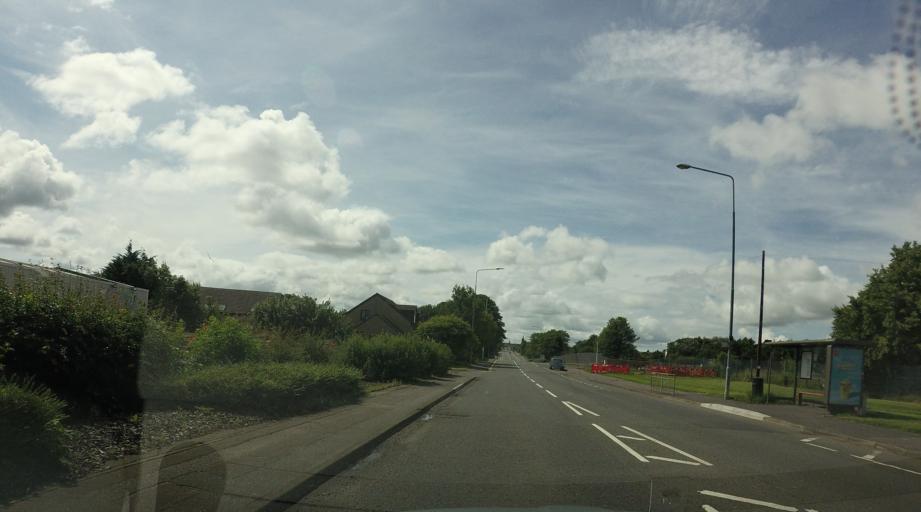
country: GB
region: Scotland
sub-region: West Lothian
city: Broxburn
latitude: 55.9343
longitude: -3.4546
